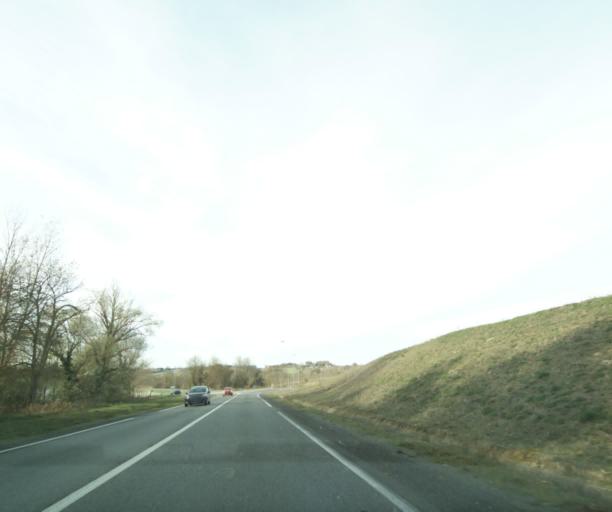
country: FR
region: Midi-Pyrenees
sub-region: Departement du Gers
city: Gimont
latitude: 43.6232
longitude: 0.9078
